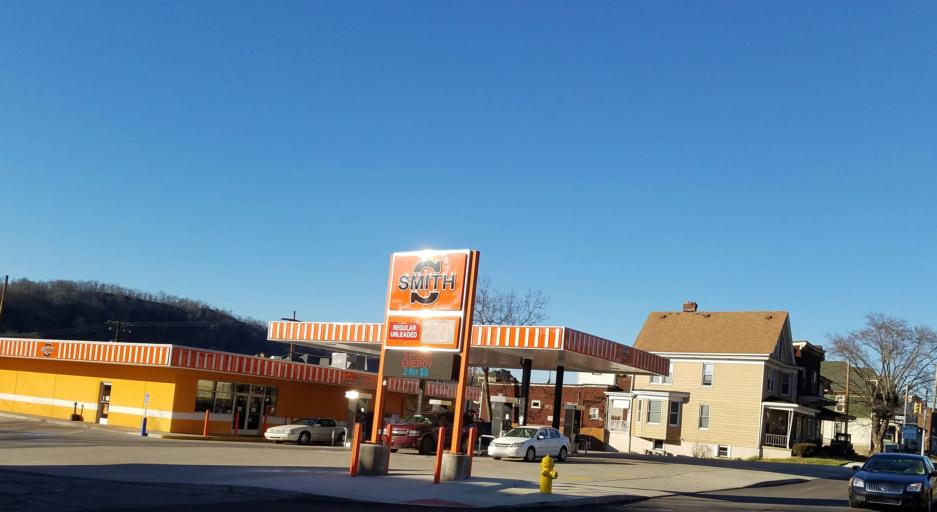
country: US
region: Ohio
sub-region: Belmont County
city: Martins Ferry
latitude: 40.1163
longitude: -80.6987
